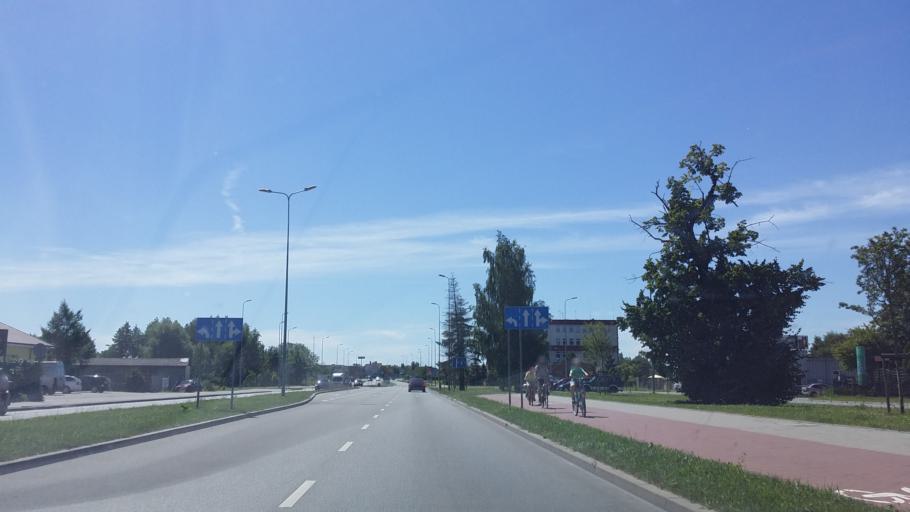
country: PL
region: West Pomeranian Voivodeship
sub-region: Powiat kolobrzeski
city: Kolobrzeg
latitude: 54.1698
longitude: 15.5548
